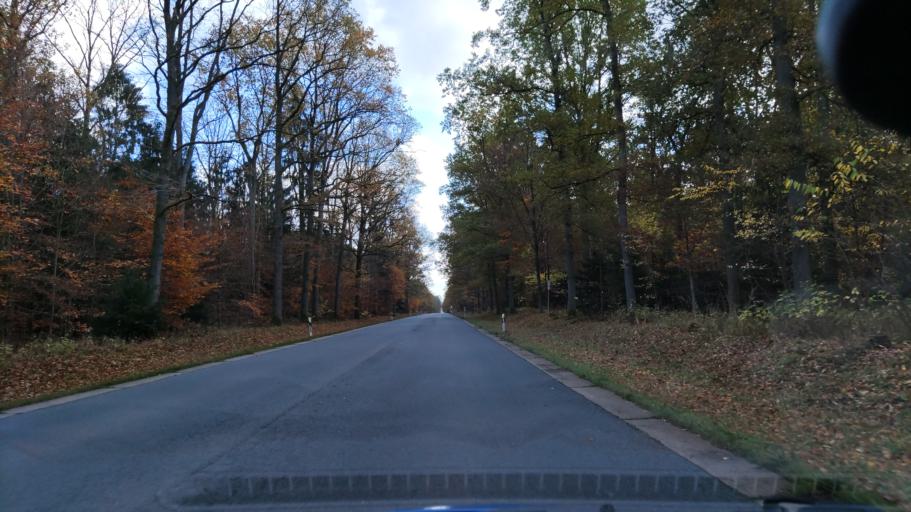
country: DE
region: Lower Saxony
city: Munster
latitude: 53.0105
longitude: 10.1031
